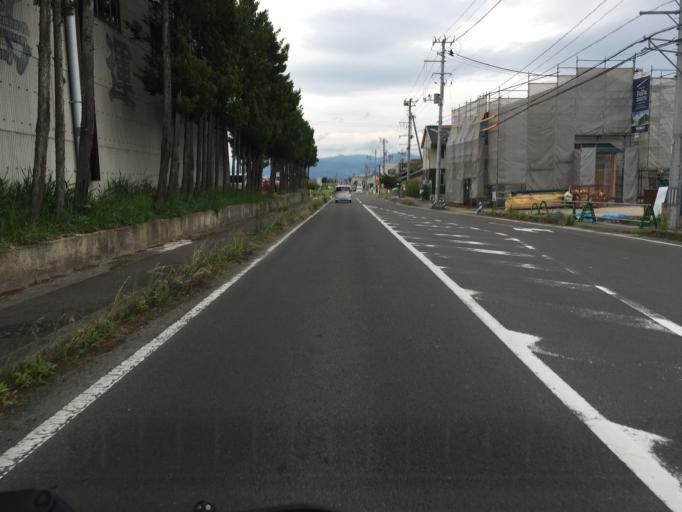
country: JP
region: Fukushima
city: Fukushima-shi
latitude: 37.7677
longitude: 140.4334
